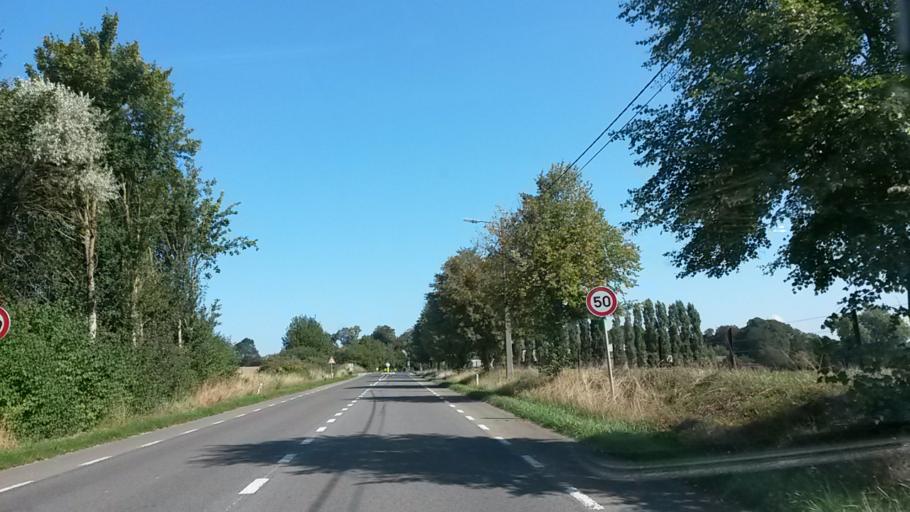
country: BE
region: Wallonia
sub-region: Province du Hainaut
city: Merbes-le-Chateau
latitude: 50.3201
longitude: 4.1503
